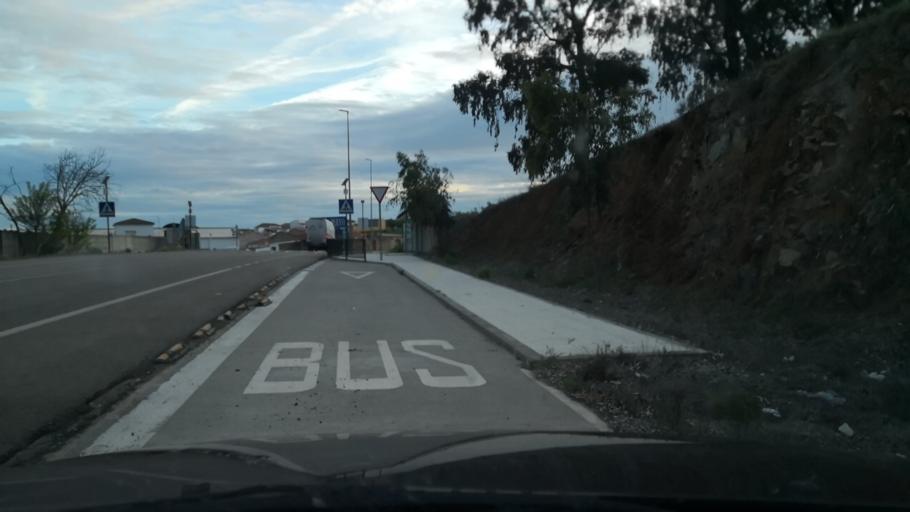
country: ES
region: Extremadura
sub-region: Provincia de Badajoz
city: La Roca de la Sierra
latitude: 39.1135
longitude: -6.6881
